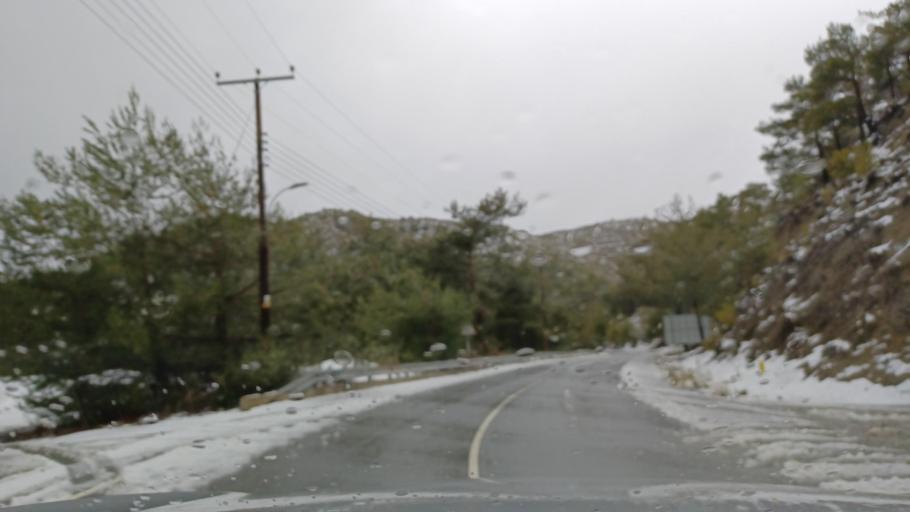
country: CY
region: Limassol
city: Pelendri
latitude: 34.8900
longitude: 32.9570
